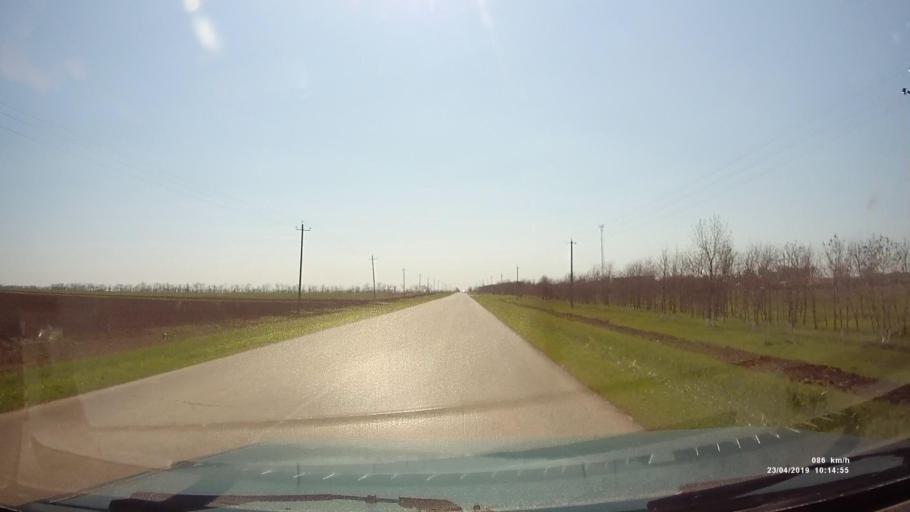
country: RU
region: Rostov
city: Sovetskoye
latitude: 46.6722
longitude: 42.3755
